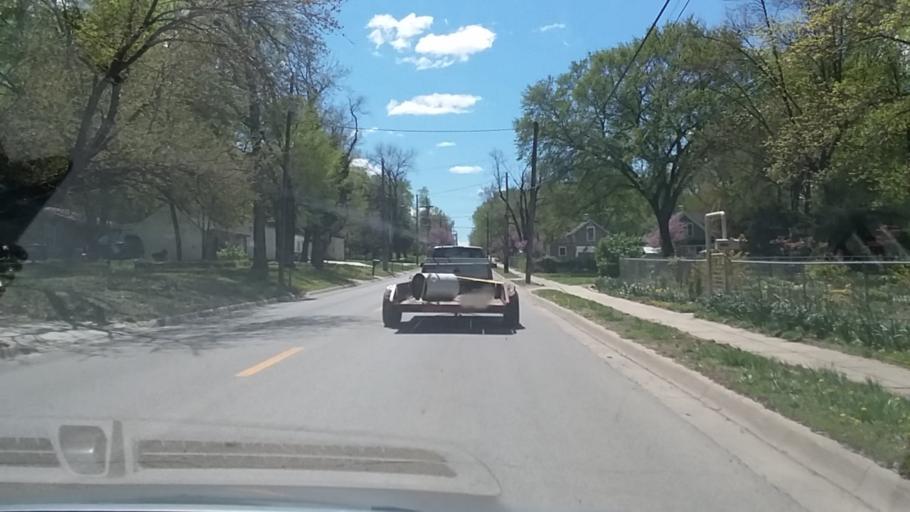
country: US
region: Kansas
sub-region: Douglas County
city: Lawrence
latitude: 38.9611
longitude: -95.2236
